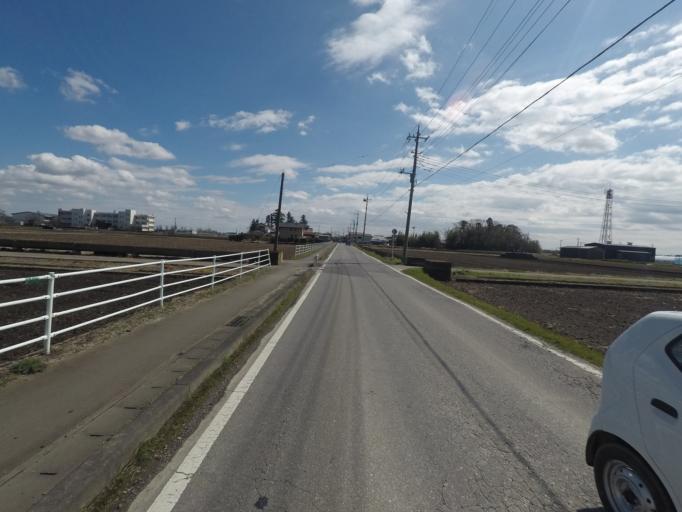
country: JP
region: Ibaraki
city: Moriya
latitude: 35.9553
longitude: 140.0563
